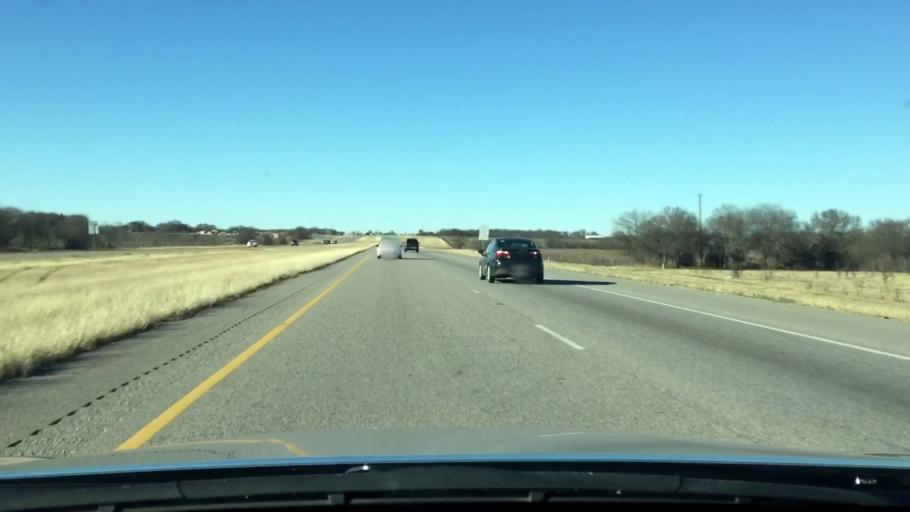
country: US
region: Texas
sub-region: Johnson County
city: Grandview
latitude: 32.2435
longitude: -97.1586
